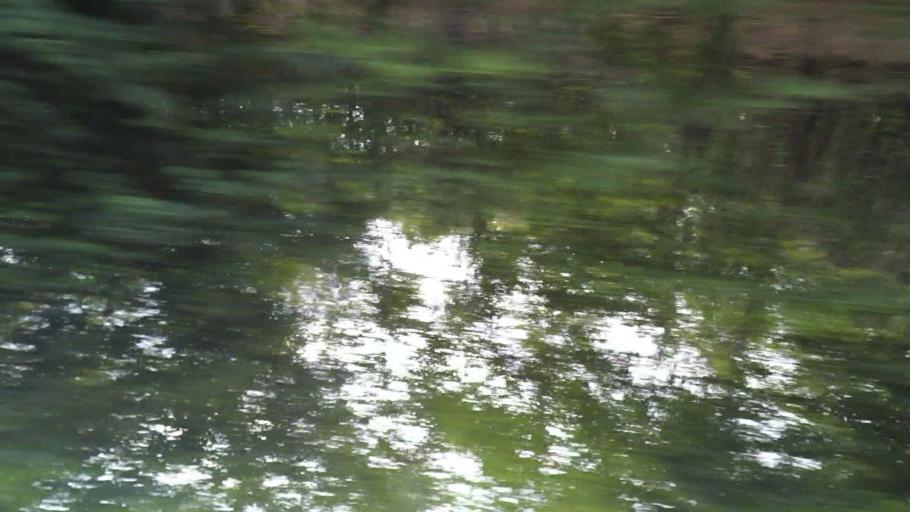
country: DK
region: Central Jutland
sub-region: Syddjurs Kommune
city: Ryomgard
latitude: 56.4409
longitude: 10.5599
